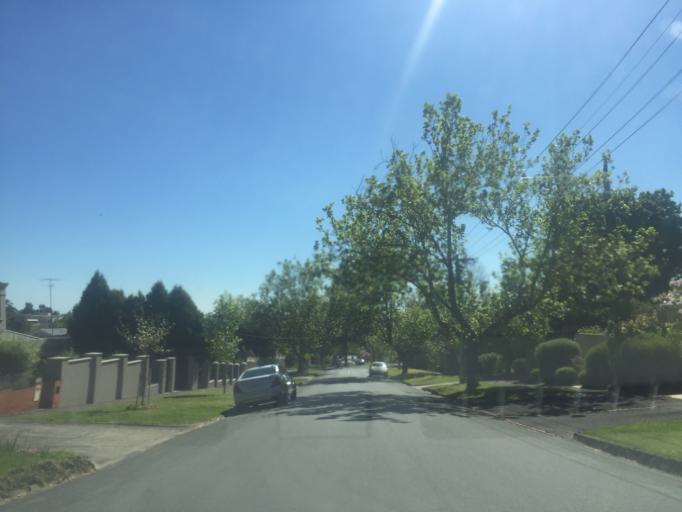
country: AU
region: Victoria
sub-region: Boroondara
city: Canterbury
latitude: -37.8111
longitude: 145.0859
